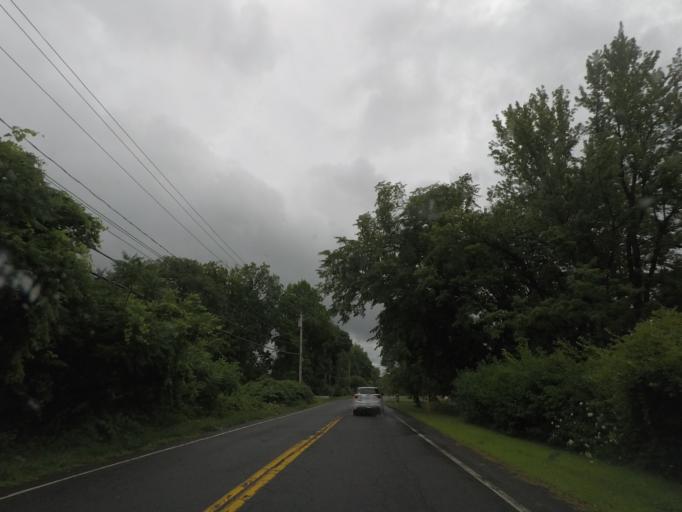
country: US
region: New York
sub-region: Rensselaer County
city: Hampton Manor
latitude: 42.6307
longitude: -73.7315
